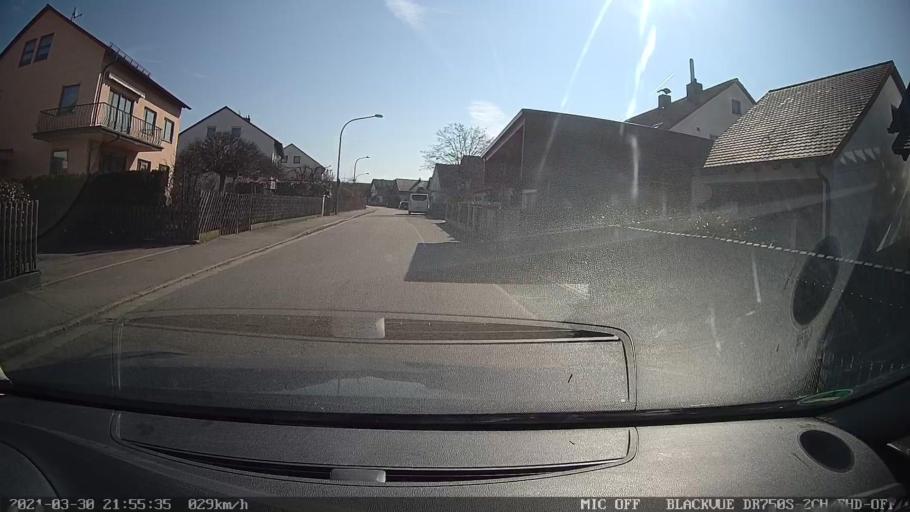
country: DE
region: Bavaria
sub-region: Upper Palatinate
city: Zeitlarn
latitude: 49.0985
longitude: 12.1146
